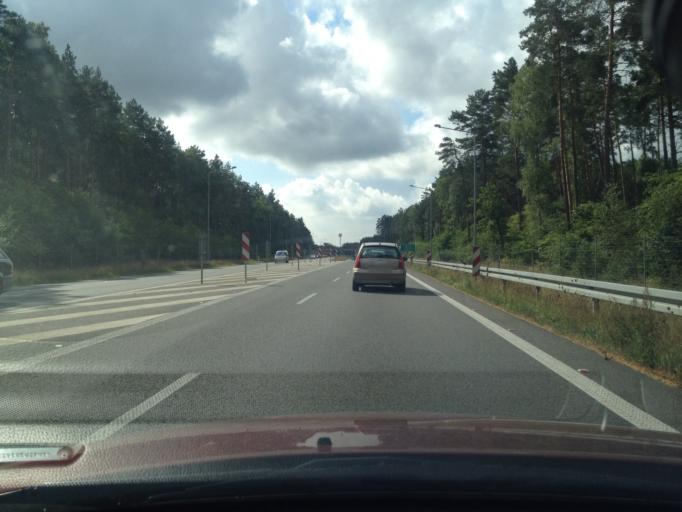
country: PL
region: West Pomeranian Voivodeship
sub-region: Powiat goleniowski
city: Goleniow
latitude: 53.6310
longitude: 14.8182
